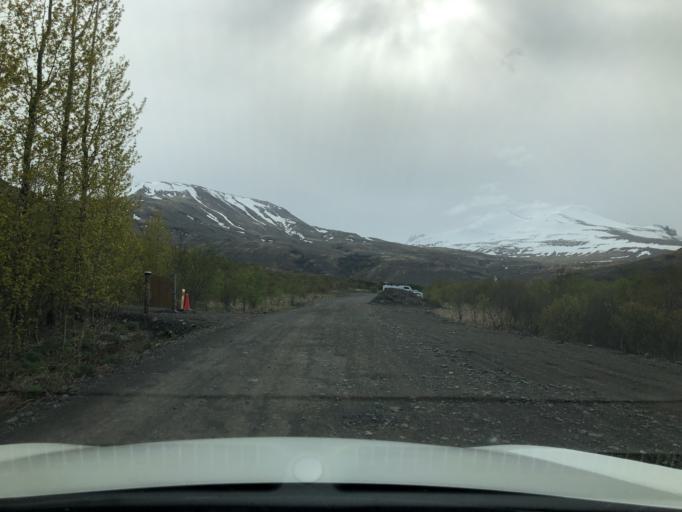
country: IS
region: South
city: Hveragerdi
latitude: 64.3856
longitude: -21.2971
